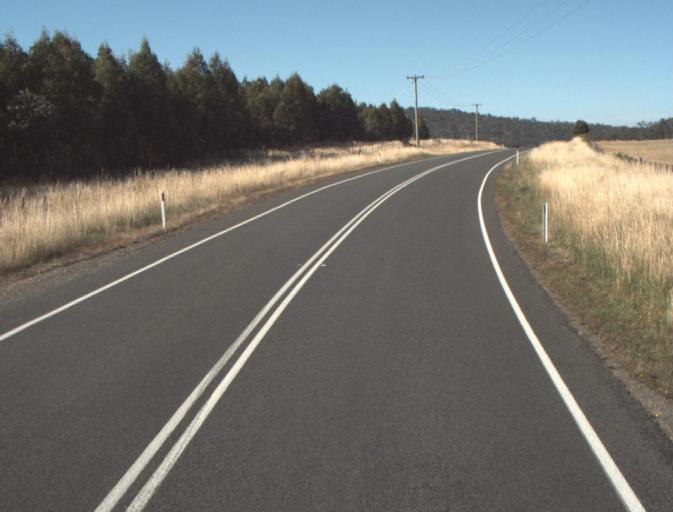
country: AU
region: Tasmania
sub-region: Launceston
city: Newstead
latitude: -41.4100
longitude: 147.2809
